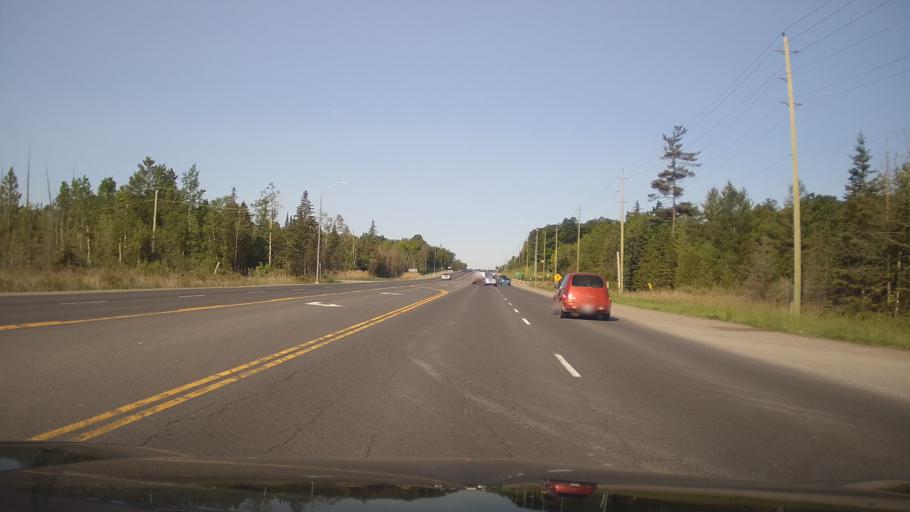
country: CA
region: Ontario
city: Peterborough
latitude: 44.3143
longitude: -78.2145
